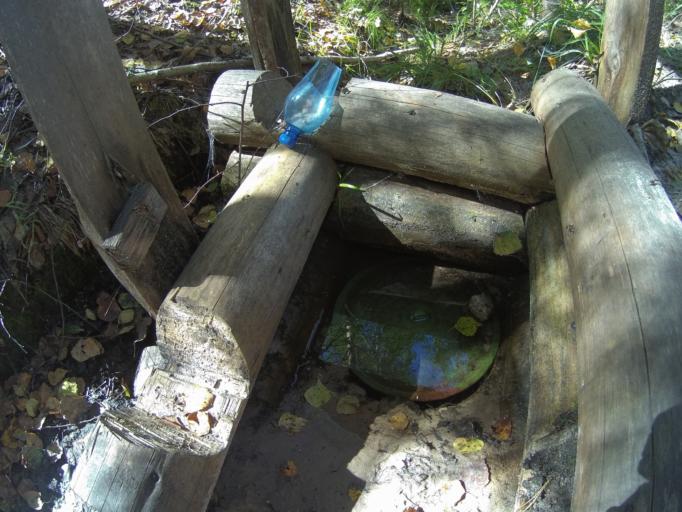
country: RU
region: Vladimir
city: Urshel'skiy
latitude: 55.7112
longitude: 40.0970
